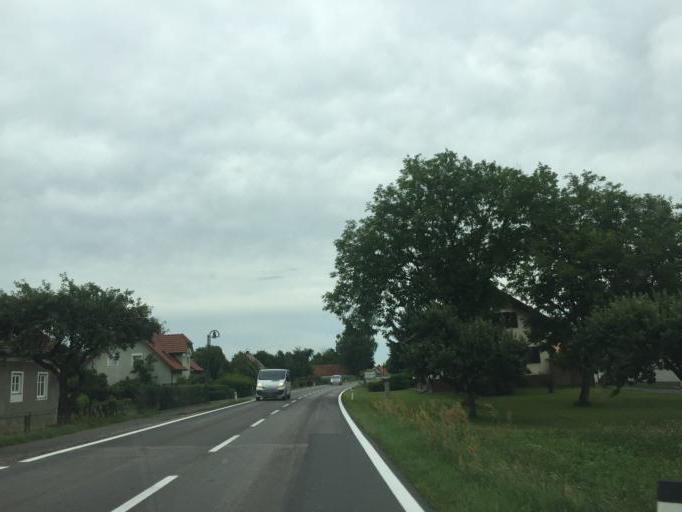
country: SI
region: Sentilj
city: Selnica ob Muri
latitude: 46.7128
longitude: 15.7155
